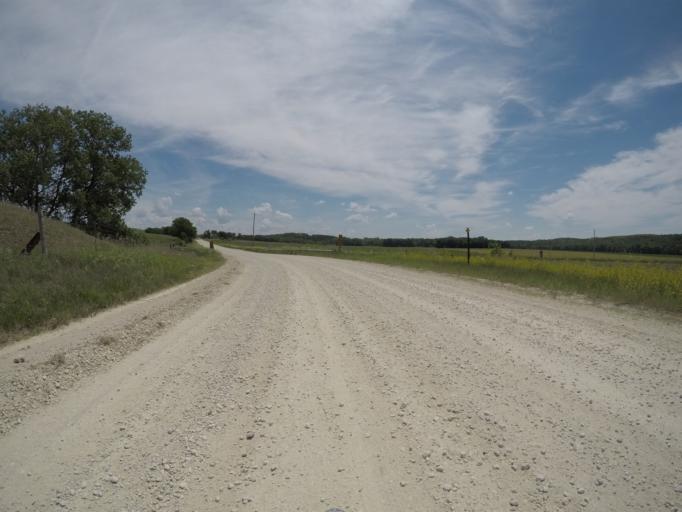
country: US
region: Kansas
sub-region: Wabaunsee County
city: Alma
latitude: 38.9652
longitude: -96.2574
